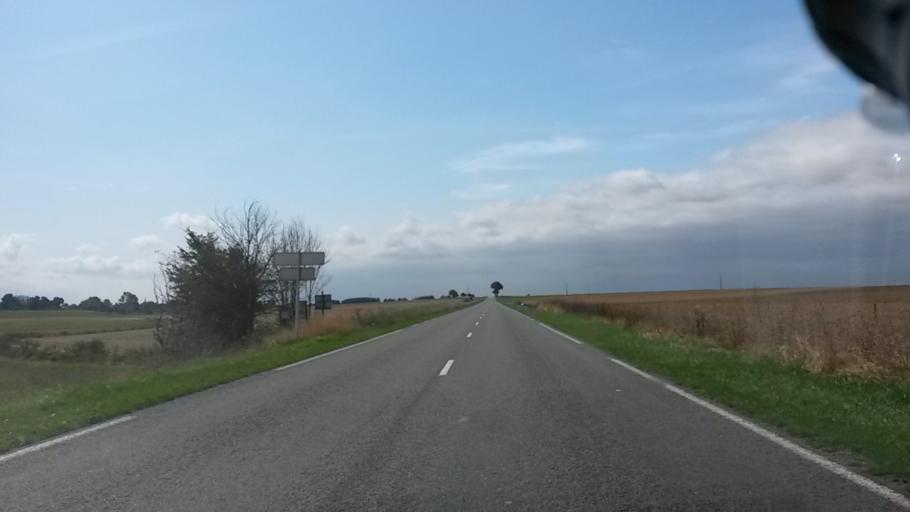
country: FR
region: Nord-Pas-de-Calais
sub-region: Departement du Pas-de-Calais
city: Hermies
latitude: 50.1340
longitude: 3.0030
